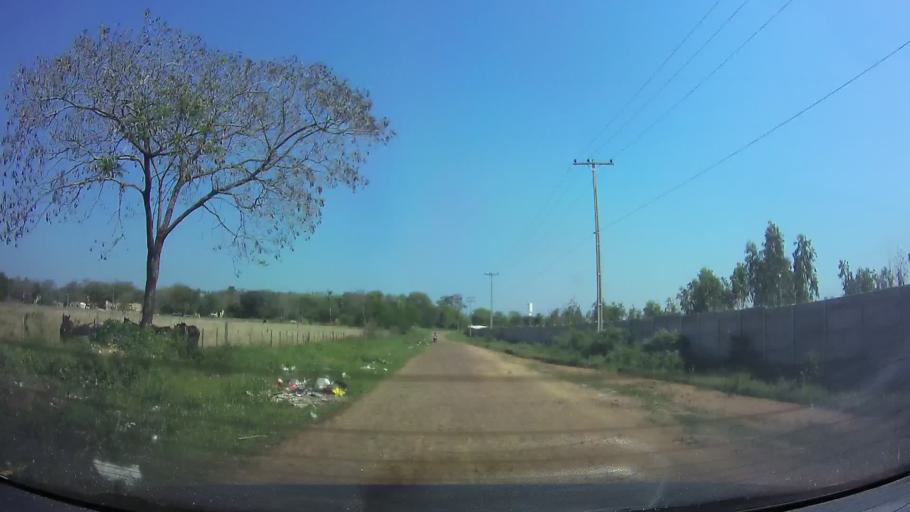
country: PY
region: Central
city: Limpio
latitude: -25.2157
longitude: -57.4837
